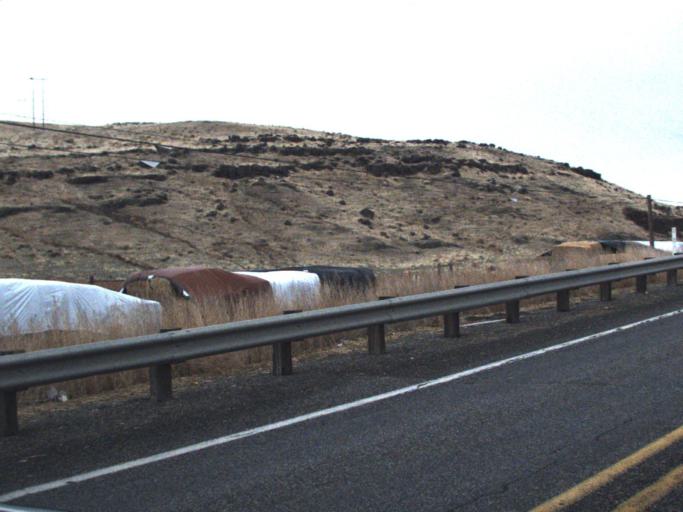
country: US
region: Washington
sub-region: Walla Walla County
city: Burbank
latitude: 46.0718
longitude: -118.7830
